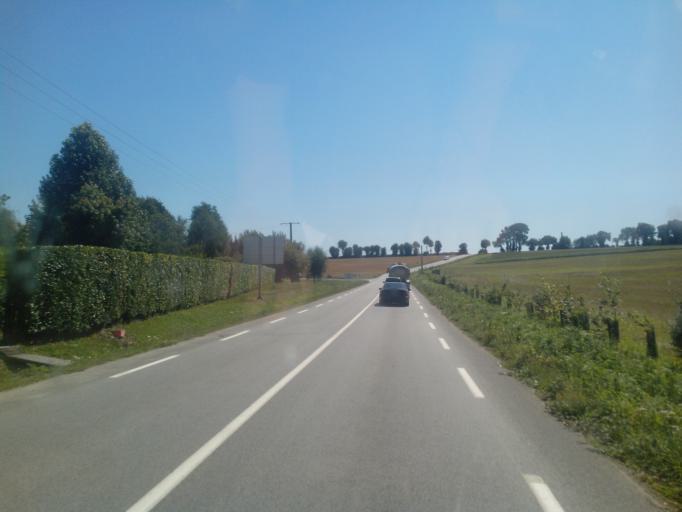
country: FR
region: Brittany
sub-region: Departement du Morbihan
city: Guillac
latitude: 47.8621
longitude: -2.4252
